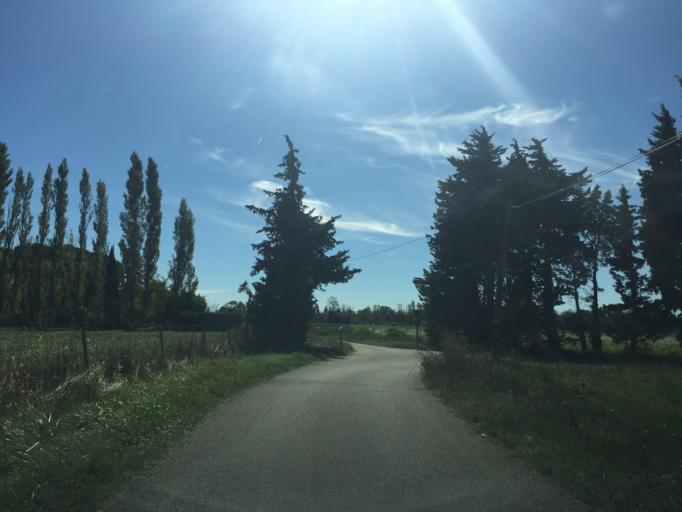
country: FR
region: Provence-Alpes-Cote d'Azur
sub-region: Departement du Vaucluse
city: Orange
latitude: 44.1536
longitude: 4.7874
